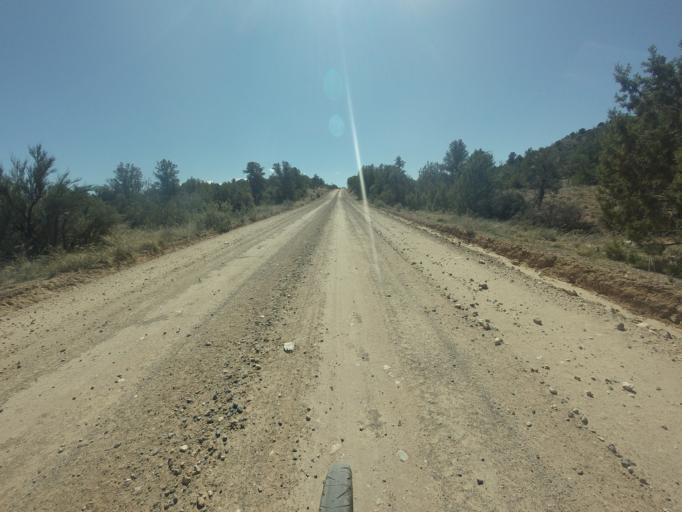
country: US
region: Arizona
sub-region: Yavapai County
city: Lake Montezuma
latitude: 34.6024
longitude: -111.7238
